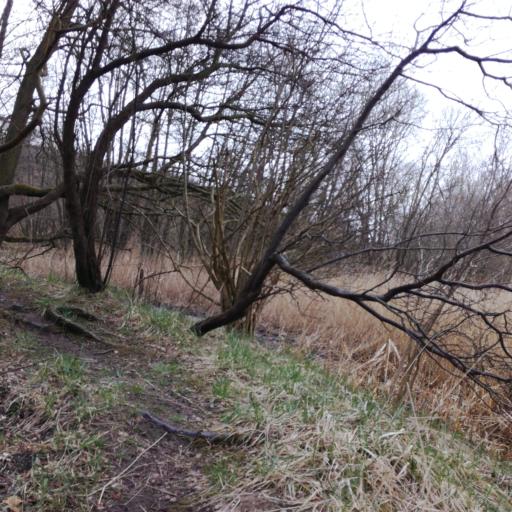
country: DK
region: South Denmark
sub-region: Fredericia Kommune
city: Fredericia
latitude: 55.6137
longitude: 9.7368
